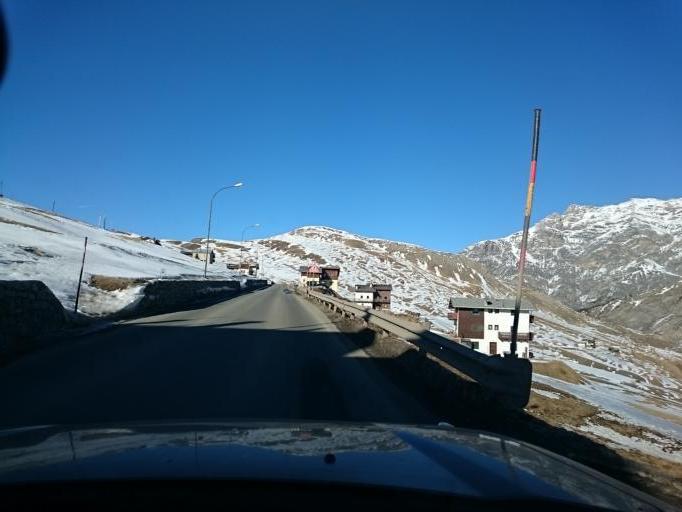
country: IT
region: Lombardy
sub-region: Provincia di Sondrio
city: Livigno
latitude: 46.5331
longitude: 10.1714
